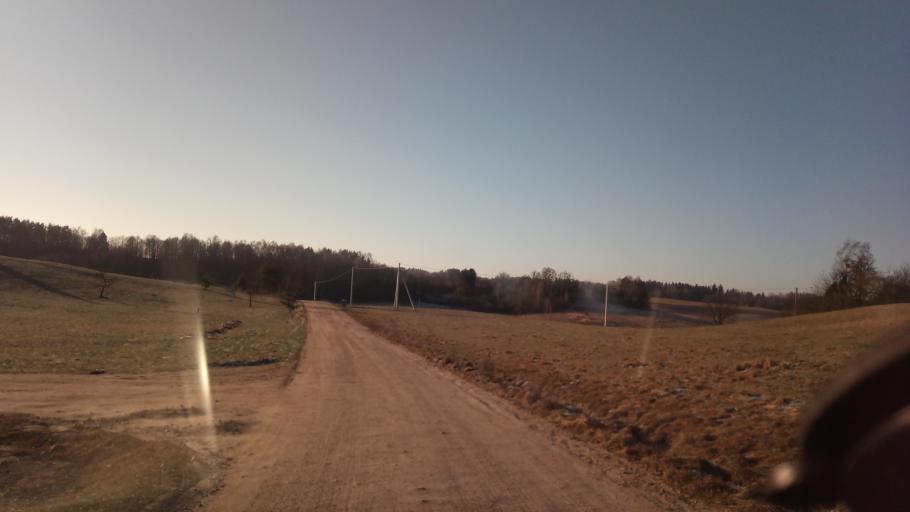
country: LT
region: Alytaus apskritis
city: Druskininkai
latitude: 54.1073
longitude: 24.0126
